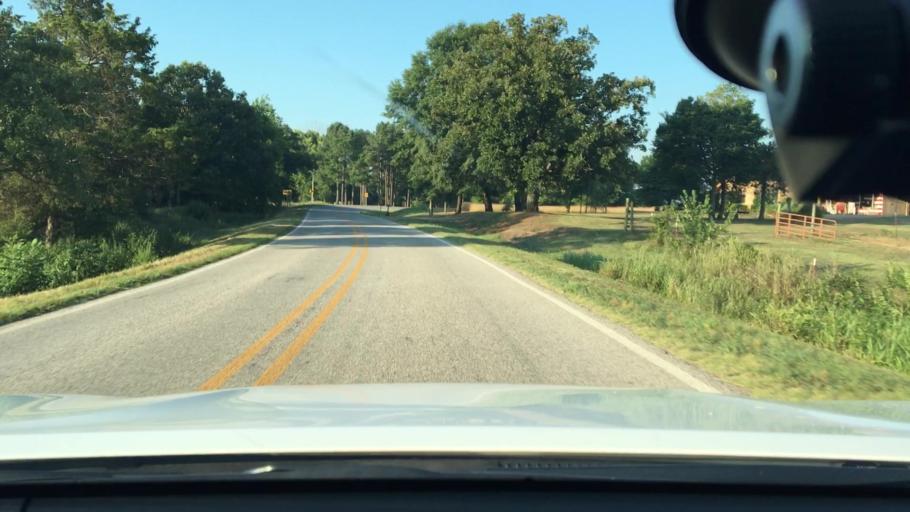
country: US
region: Arkansas
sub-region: Johnson County
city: Coal Hill
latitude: 35.3427
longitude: -93.5962
